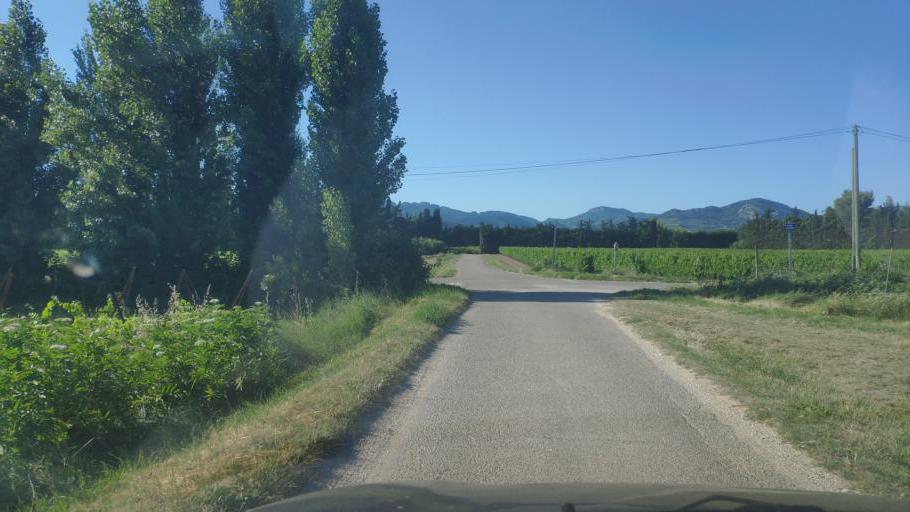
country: FR
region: Provence-Alpes-Cote d'Azur
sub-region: Departement du Vaucluse
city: Aubignan
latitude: 44.0870
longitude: 5.0402
